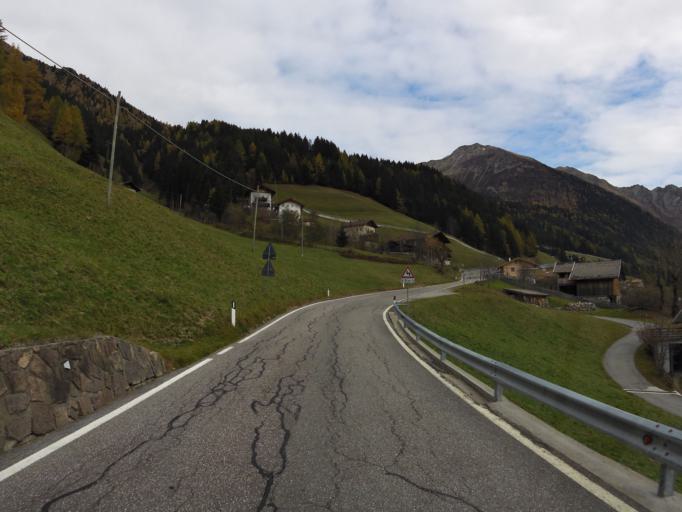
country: IT
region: Trentino-Alto Adige
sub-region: Bolzano
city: Racines
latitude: 46.8266
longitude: 11.2901
